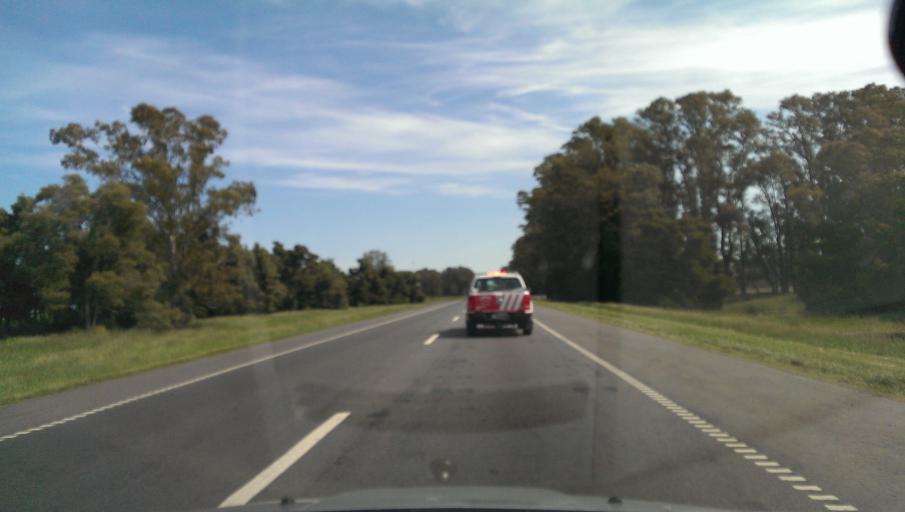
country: AR
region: Buenos Aires
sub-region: Partido de Las Flores
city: Las Flores
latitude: -36.3785
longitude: -59.4802
